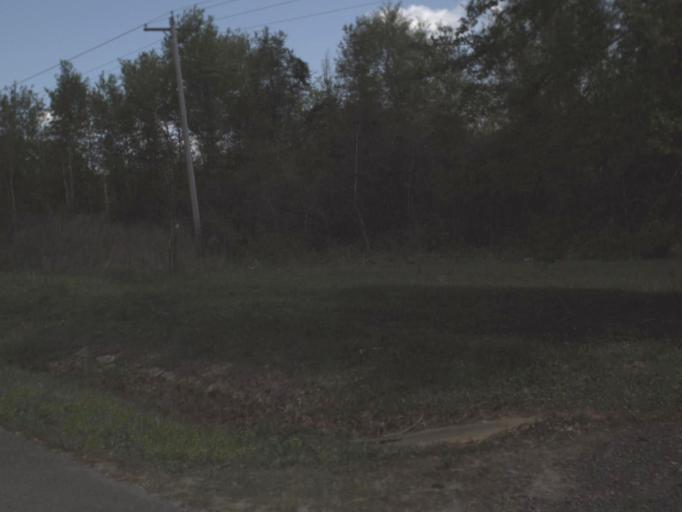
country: US
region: Alabama
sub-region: Escambia County
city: East Brewton
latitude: 30.9250
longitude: -87.0517
